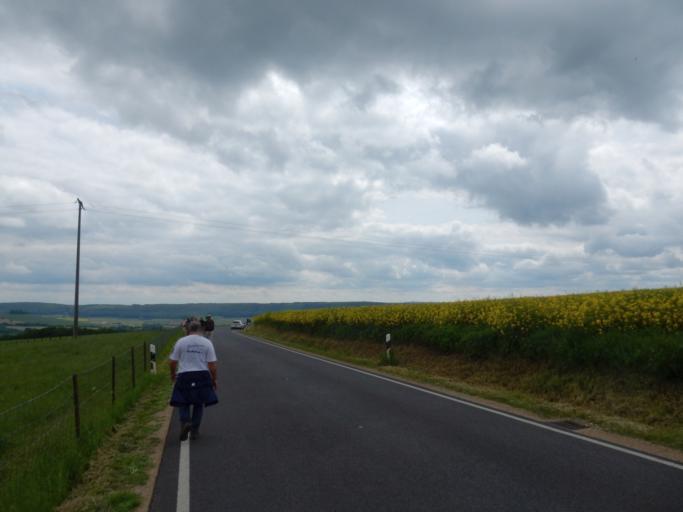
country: LU
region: Diekirch
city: Warken
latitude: 49.8737
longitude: 6.0940
